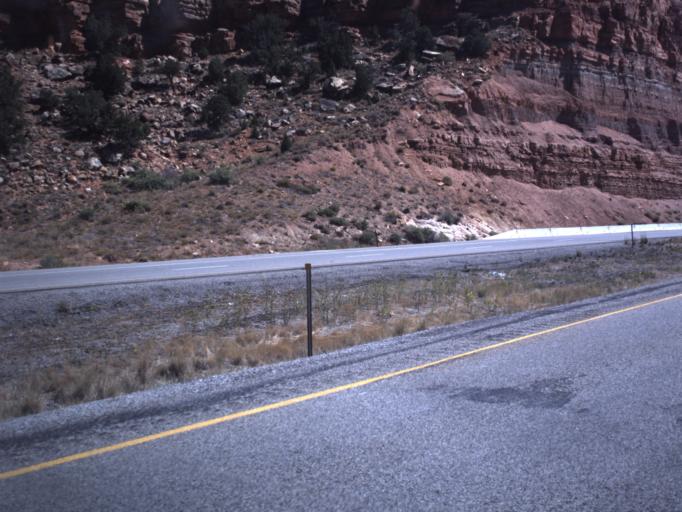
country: US
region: Utah
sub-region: Sevier County
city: Salina
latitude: 38.9321
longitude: -111.7899
